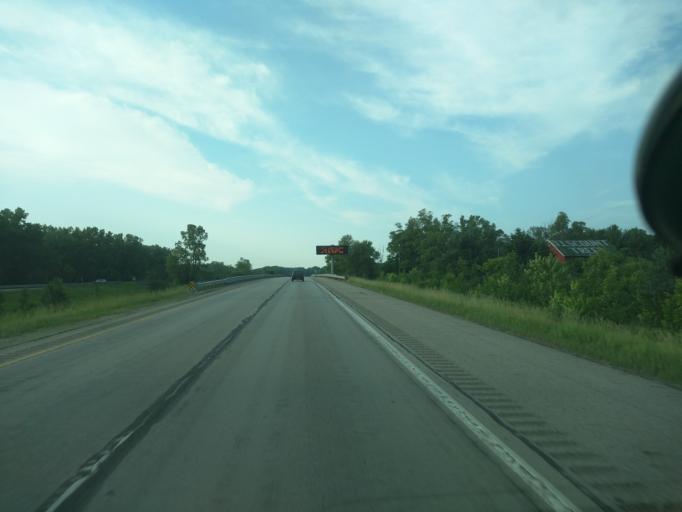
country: US
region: Michigan
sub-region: Ingham County
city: Holt
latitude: 42.6529
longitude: -84.4757
